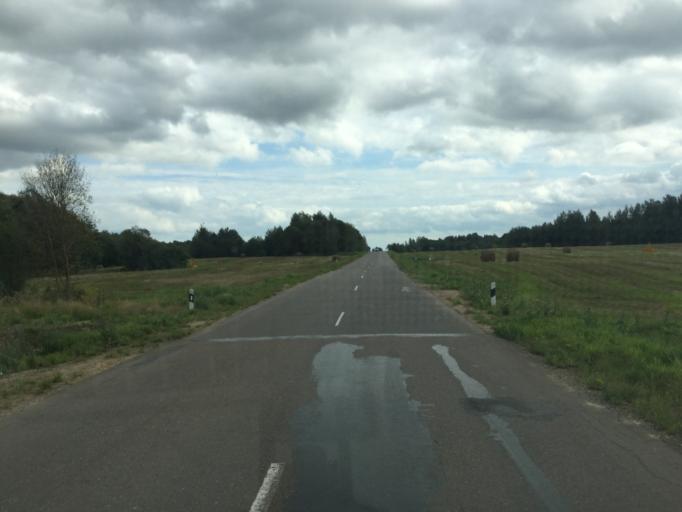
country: BY
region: Vitebsk
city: Vitebsk
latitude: 55.1319
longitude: 30.3105
